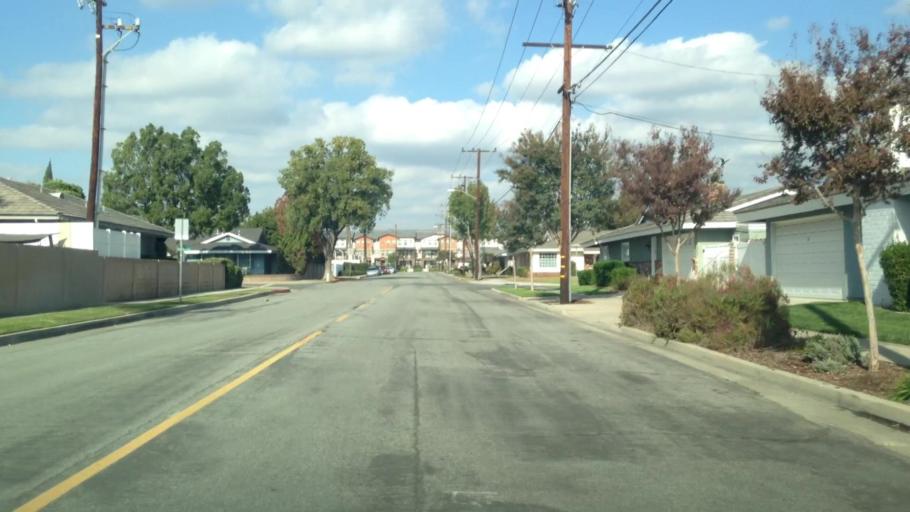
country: US
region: California
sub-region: Orange County
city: Yorba Linda
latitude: 33.8859
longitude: -117.8373
